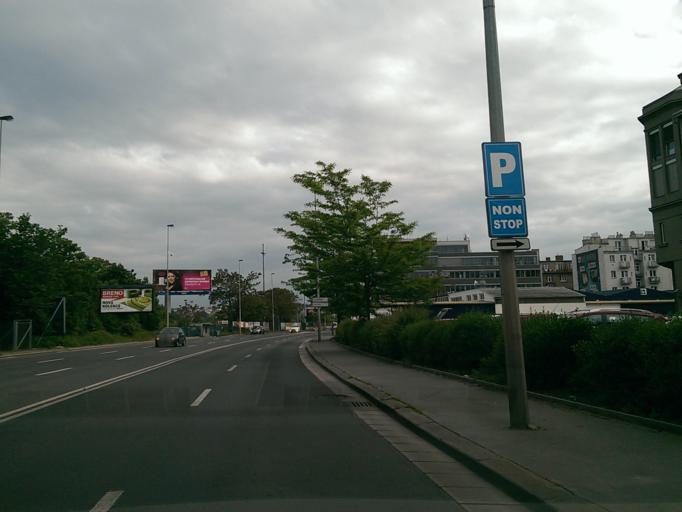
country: CZ
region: Praha
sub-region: Praha 2
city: Vysehrad
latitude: 50.0617
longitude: 14.4110
